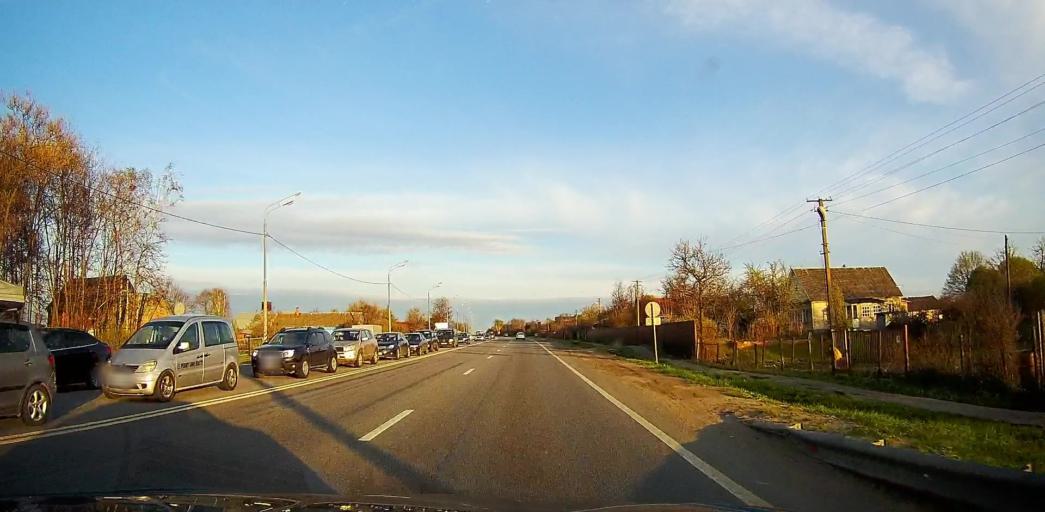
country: RU
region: Moskovskaya
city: Troitskoye
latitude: 55.2466
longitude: 38.5300
